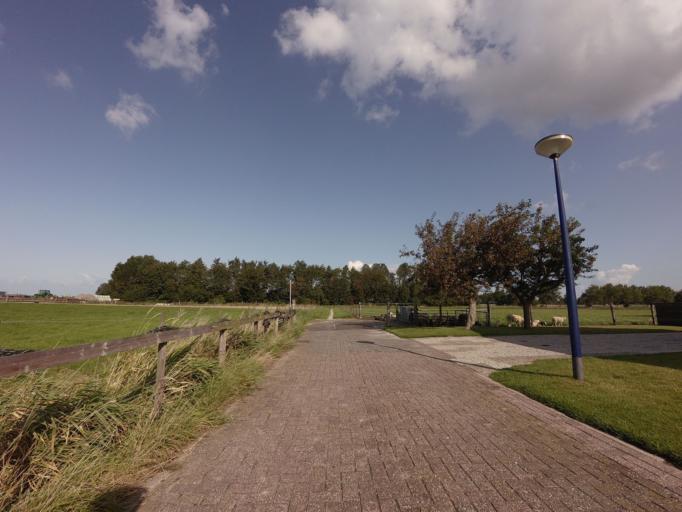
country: NL
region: Friesland
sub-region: Gemeente Franekeradeel
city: Tzummarum
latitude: 53.2380
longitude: 5.5391
